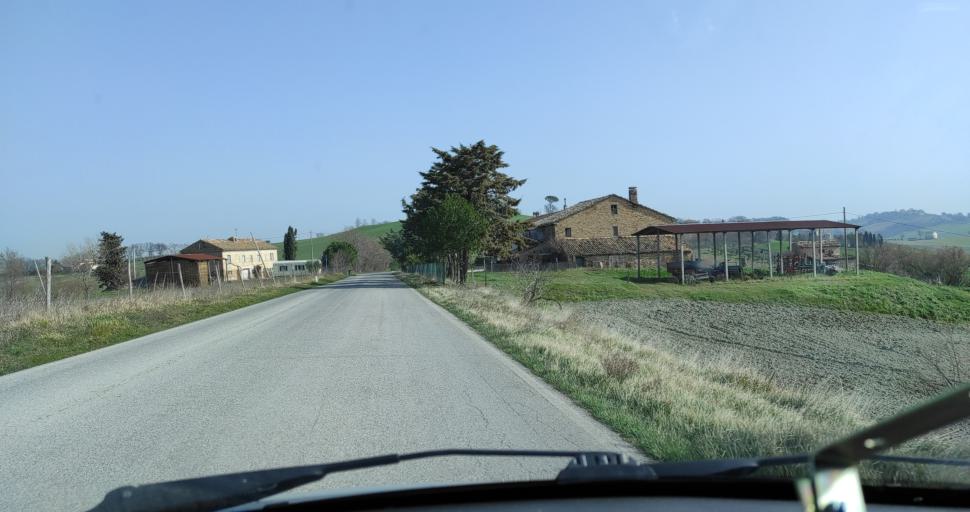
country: IT
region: The Marches
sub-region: Provincia di Macerata
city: Loro Piceno
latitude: 43.1775
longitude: 13.4397
